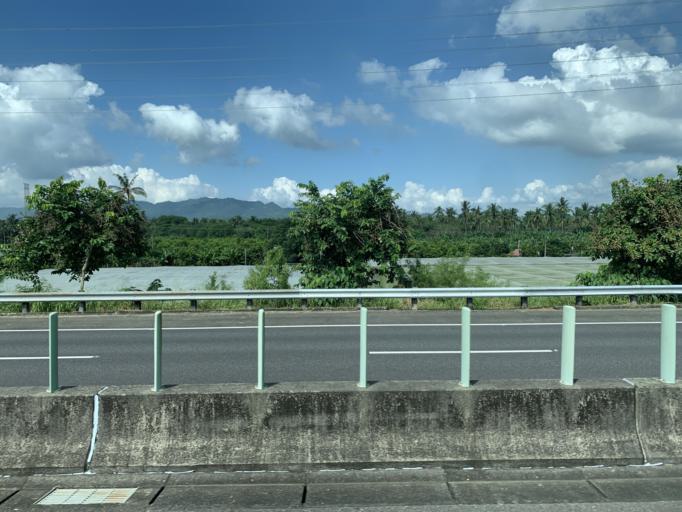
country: TW
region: Taiwan
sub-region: Pingtung
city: Pingtung
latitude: 22.8401
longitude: 120.4956
